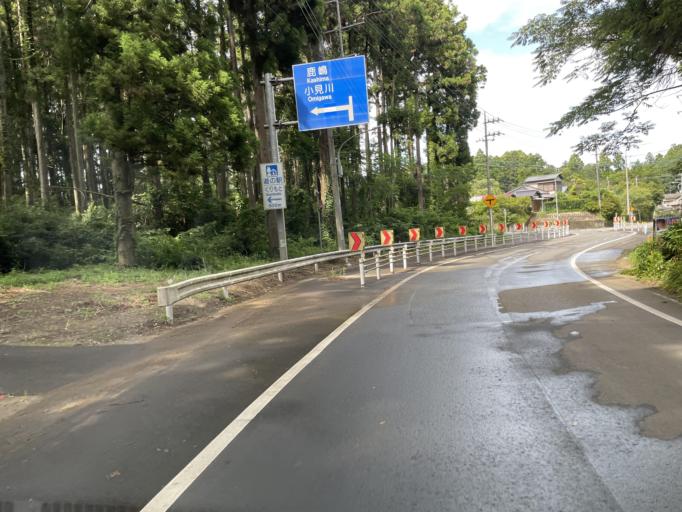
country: JP
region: Chiba
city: Sawara
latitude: 35.8012
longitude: 140.4680
